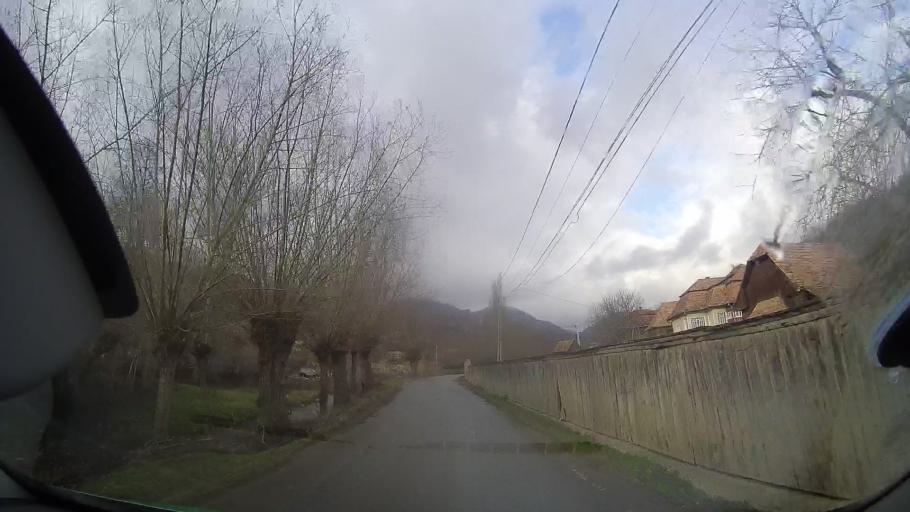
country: RO
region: Alba
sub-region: Comuna Ocolis
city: Ocolis
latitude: 46.4839
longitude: 23.4623
